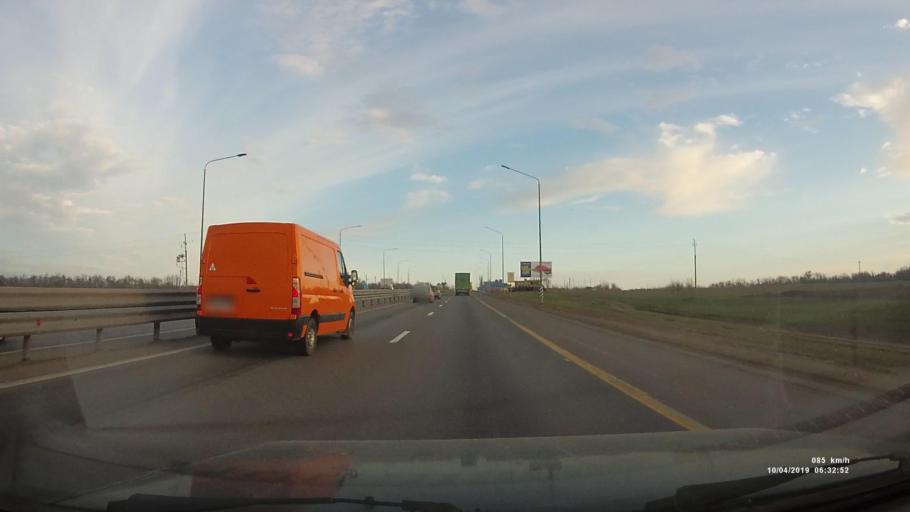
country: RU
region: Rostov
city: Aksay
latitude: 47.2805
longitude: 39.8508
